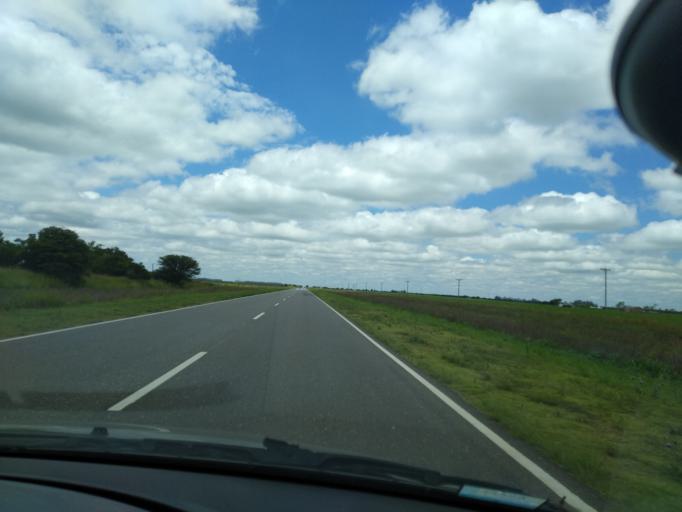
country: AR
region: Cordoba
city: Toledo
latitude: -31.6454
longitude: -64.0205
